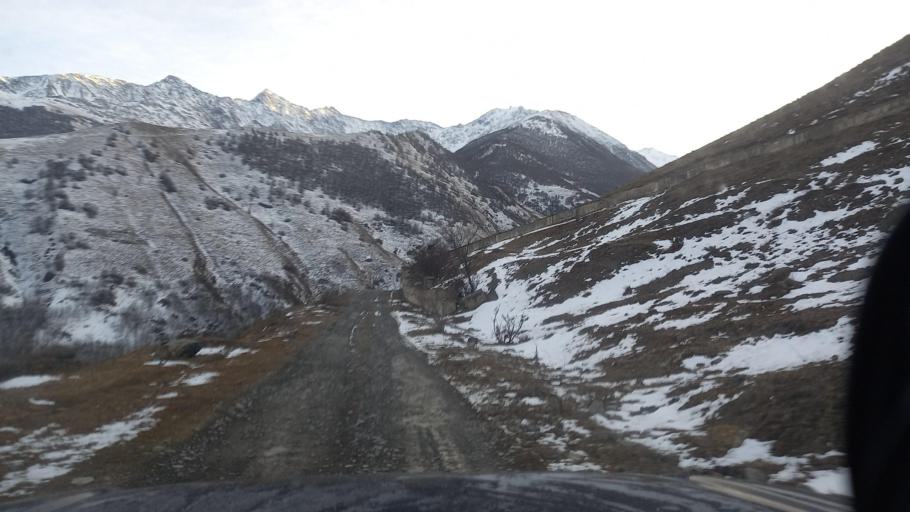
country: RU
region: Ingushetiya
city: Dzhayrakh
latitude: 42.8420
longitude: 44.5123
